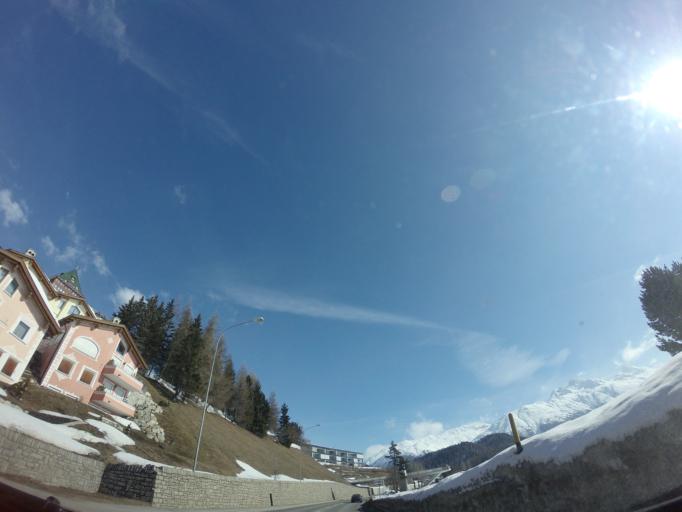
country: CH
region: Grisons
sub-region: Maloja District
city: Saint Moritz
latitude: 46.4956
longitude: 9.8408
